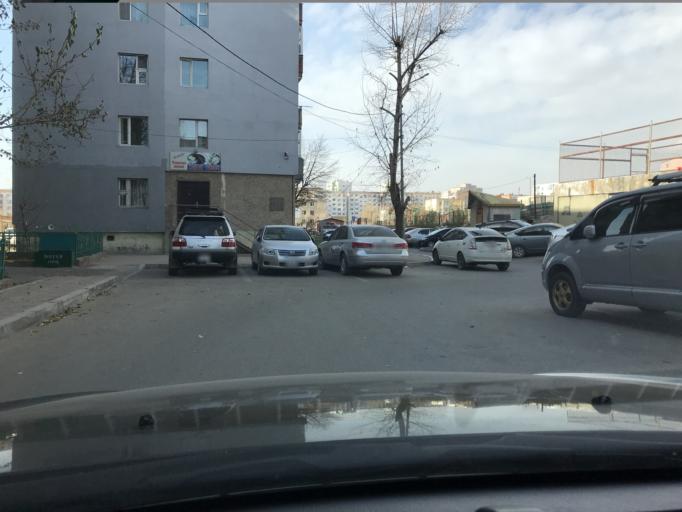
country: MN
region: Ulaanbaatar
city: Ulaanbaatar
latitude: 47.9226
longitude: 106.9470
